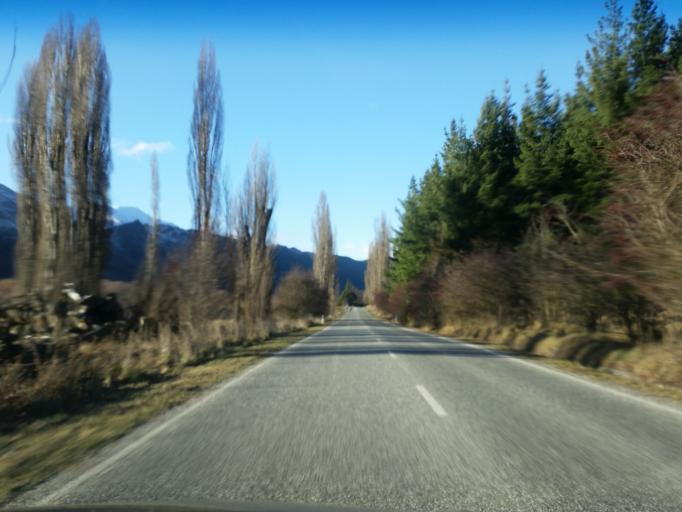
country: NZ
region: Otago
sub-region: Queenstown-Lakes District
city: Arrowtown
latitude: -44.9580
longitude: 168.7305
